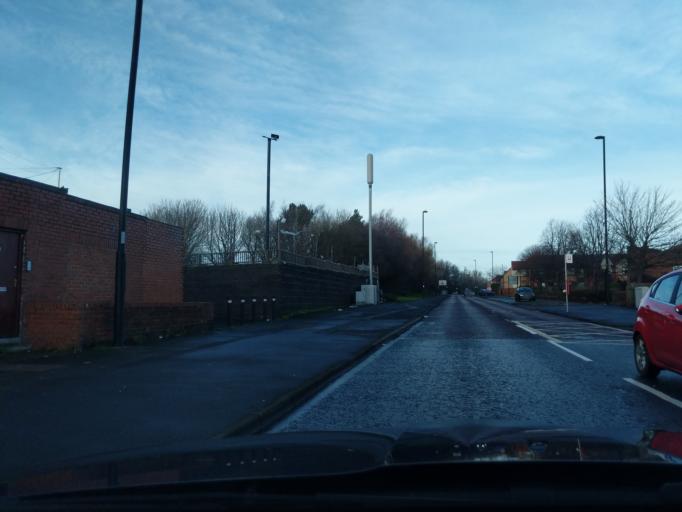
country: GB
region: England
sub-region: Gateshead
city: Felling
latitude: 54.9717
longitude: -1.5696
